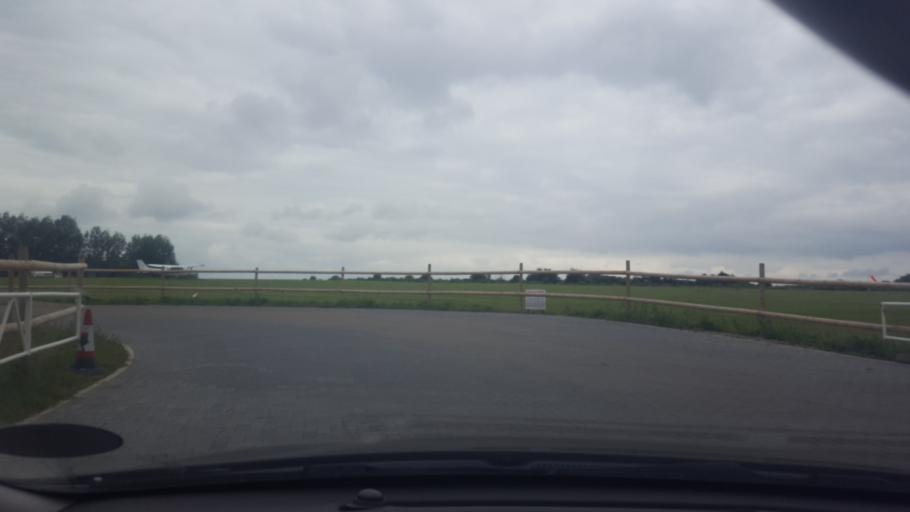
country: GB
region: England
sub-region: Essex
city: Clacton-on-Sea
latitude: 51.7824
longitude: 1.1288
